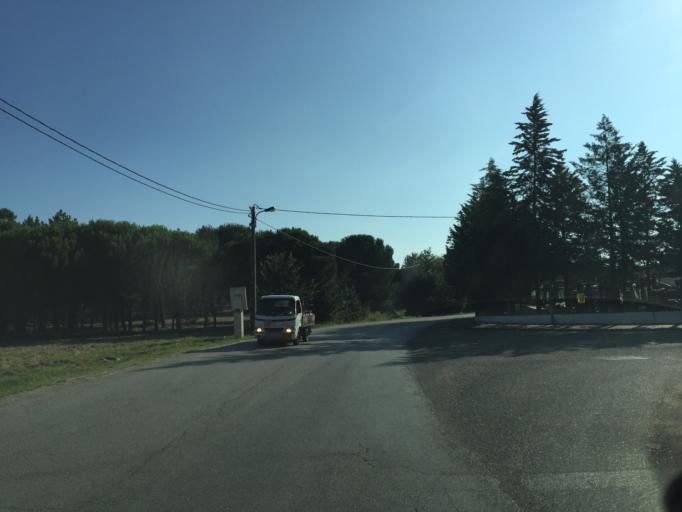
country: PT
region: Santarem
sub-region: Abrantes
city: Alferrarede
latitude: 39.4846
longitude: -8.1846
